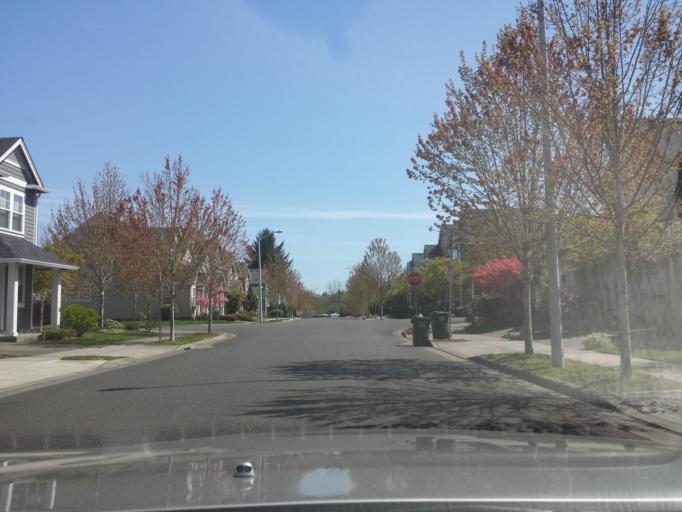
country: US
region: Oregon
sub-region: Washington County
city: Aloha
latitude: 45.4854
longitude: -122.8597
